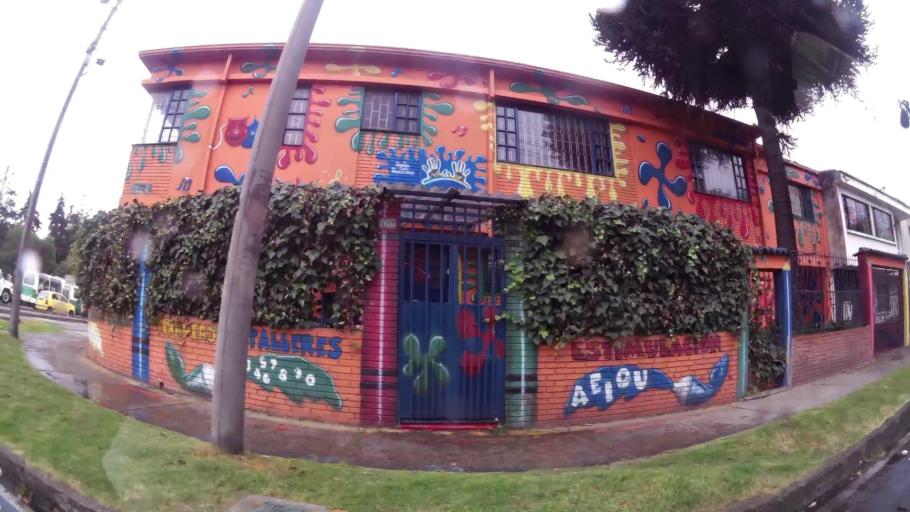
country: CO
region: Bogota D.C.
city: Bogota
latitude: 4.6547
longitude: -74.1022
